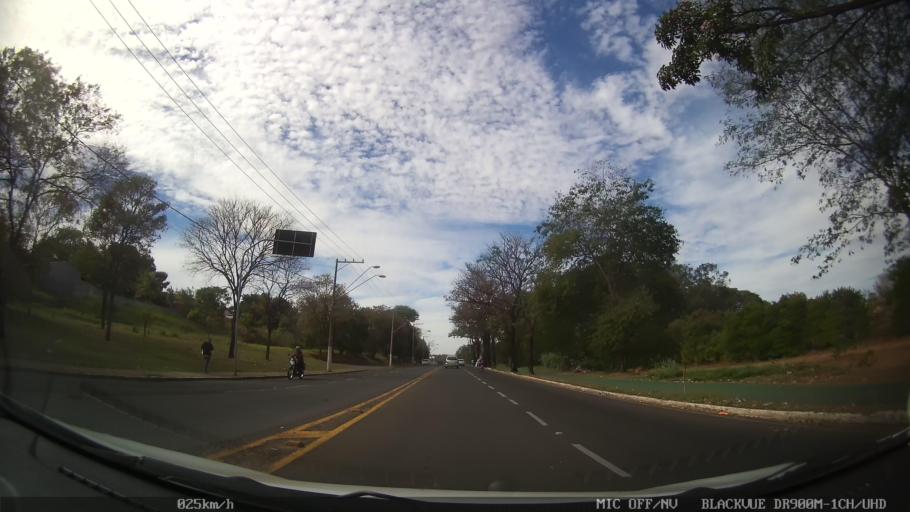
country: BR
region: Sao Paulo
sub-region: Catanduva
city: Catanduva
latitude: -21.1383
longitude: -48.9648
